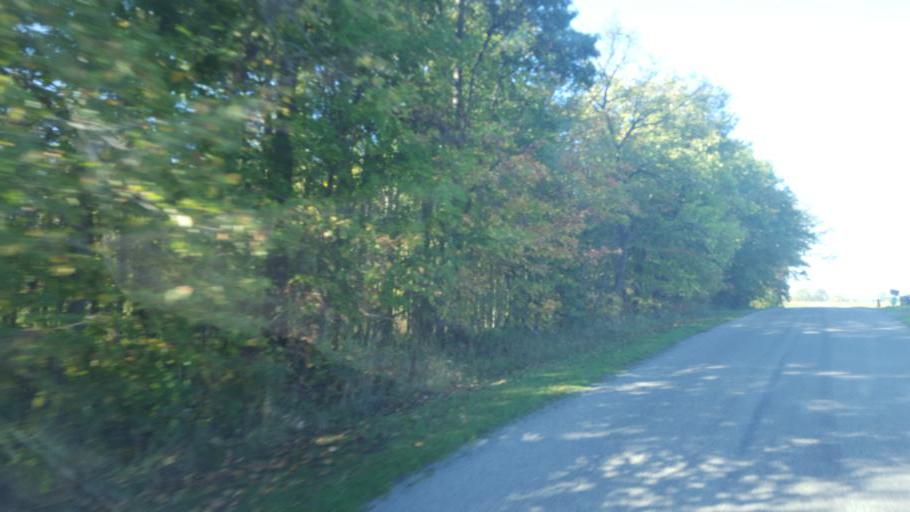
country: US
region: Ohio
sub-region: Union County
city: Richwood
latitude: 40.4951
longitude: -83.4646
